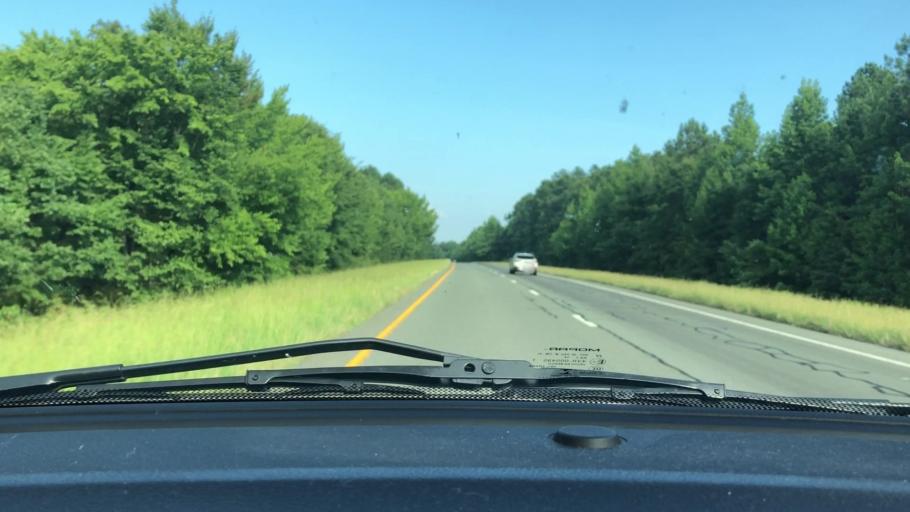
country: US
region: North Carolina
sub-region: Randolph County
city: Liberty
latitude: 35.7866
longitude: -79.5212
